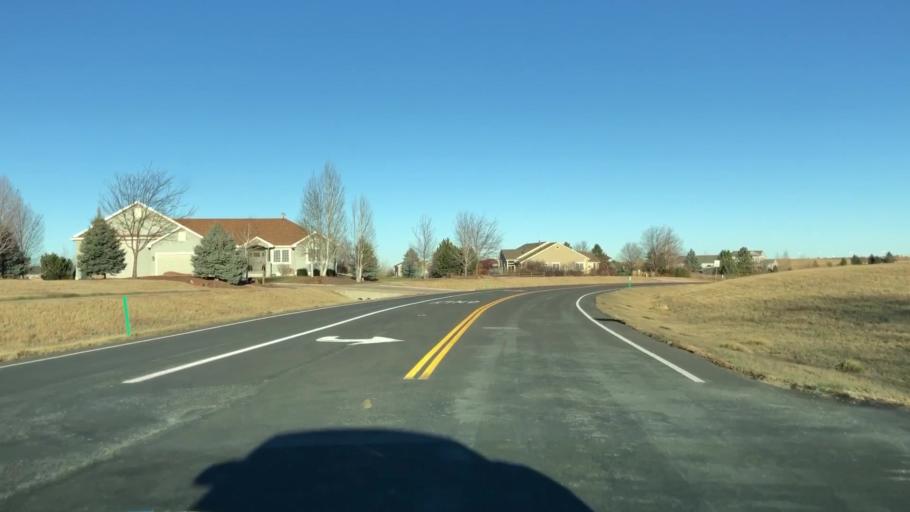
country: US
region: Colorado
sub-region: Weld County
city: Windsor
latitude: 40.4454
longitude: -104.9508
